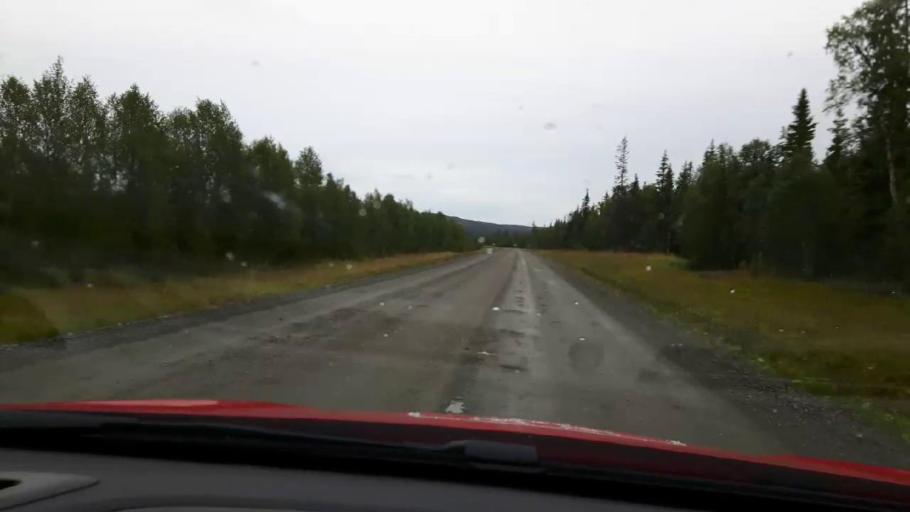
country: NO
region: Nord-Trondelag
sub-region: Meraker
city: Meraker
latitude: 63.5570
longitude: 12.3172
